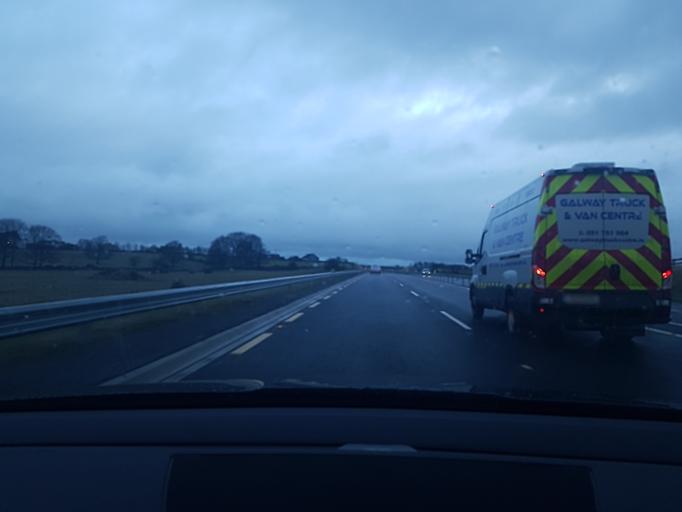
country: IE
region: Connaught
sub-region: County Galway
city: Tuam
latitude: 53.5292
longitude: -8.8658
